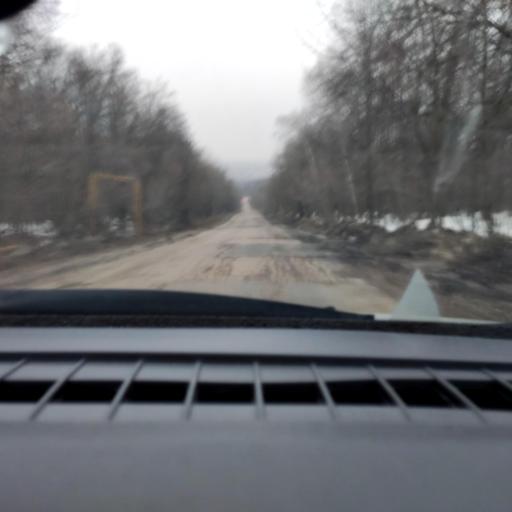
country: RU
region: Samara
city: Novosemeykino
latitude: 53.3333
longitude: 50.2599
